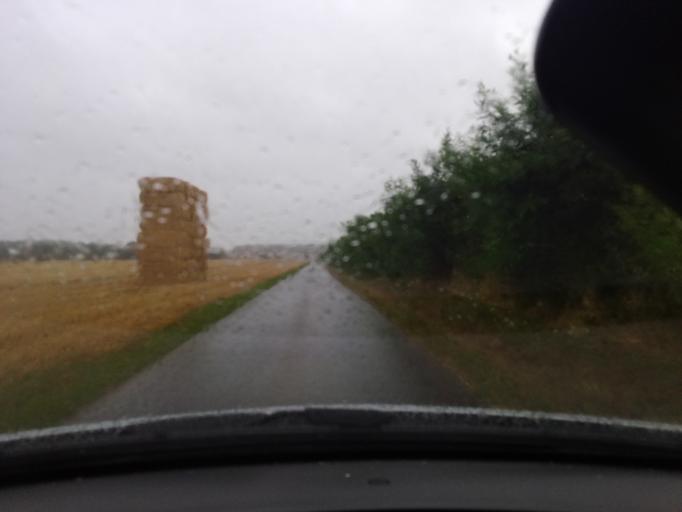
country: FR
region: Pays de la Loire
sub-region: Departement de la Vendee
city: Sainte-Gemme-la-Plaine
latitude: 46.4898
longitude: -1.1190
